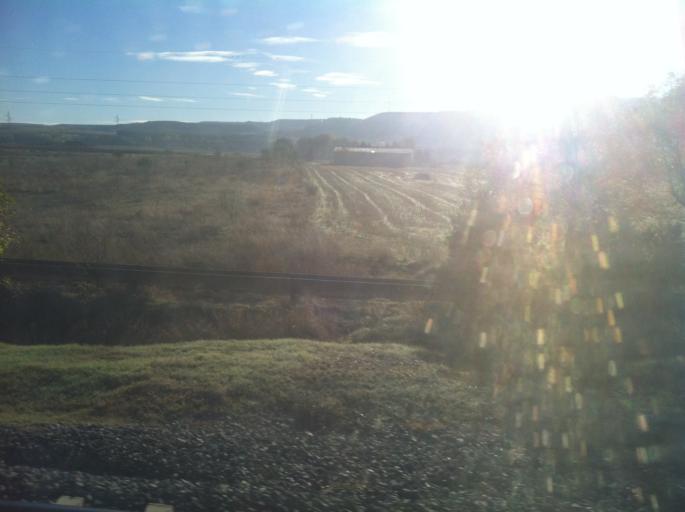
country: ES
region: Castille and Leon
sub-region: Provincia de Valladolid
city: Cabezon
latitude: 41.7198
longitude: -4.6631
